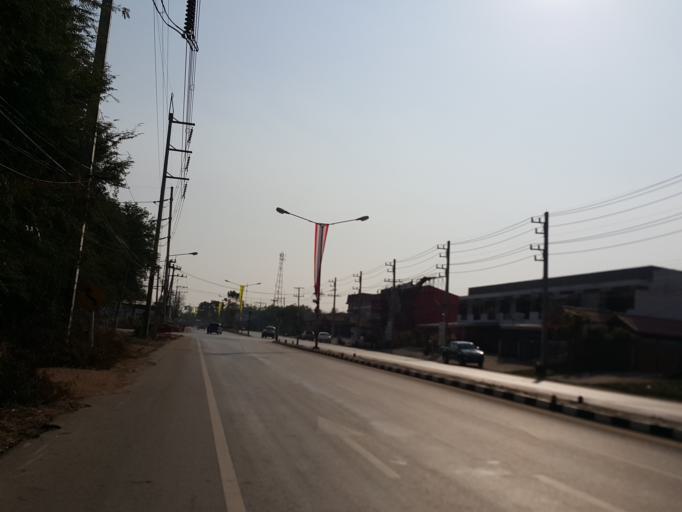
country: TH
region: Lampang
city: Lampang
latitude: 18.3444
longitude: 99.5362
